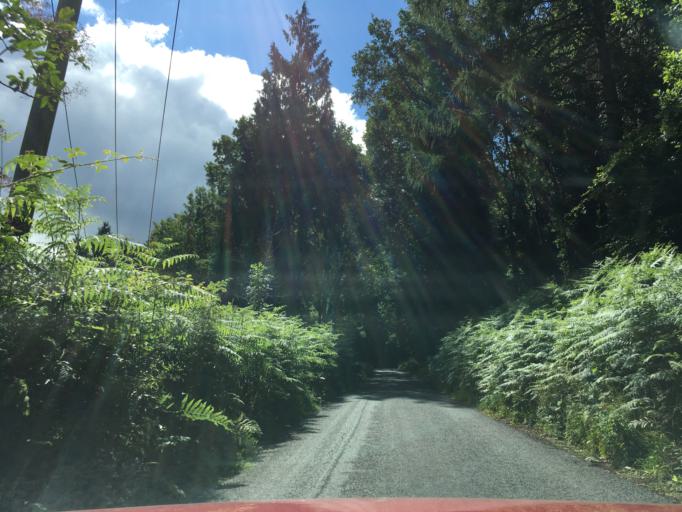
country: GB
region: England
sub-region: Gloucestershire
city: Cinderford
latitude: 51.7902
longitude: -2.5026
